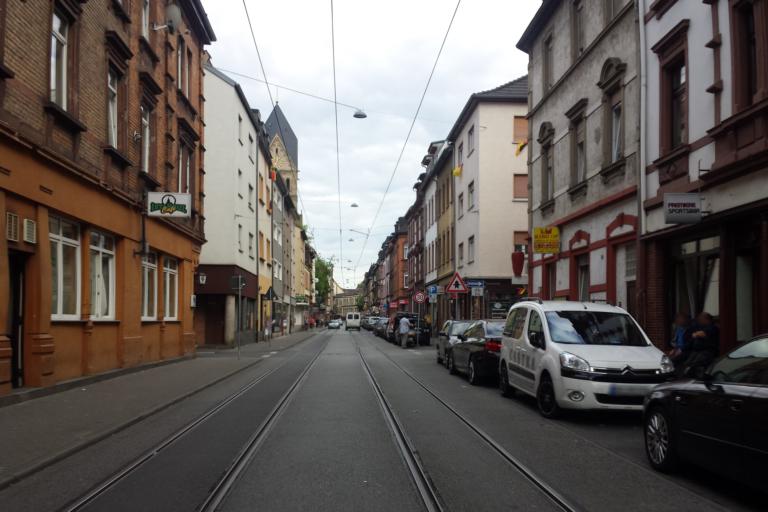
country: DE
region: Baden-Wuerttemberg
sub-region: Karlsruhe Region
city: Mannheim
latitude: 49.5008
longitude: 8.4644
